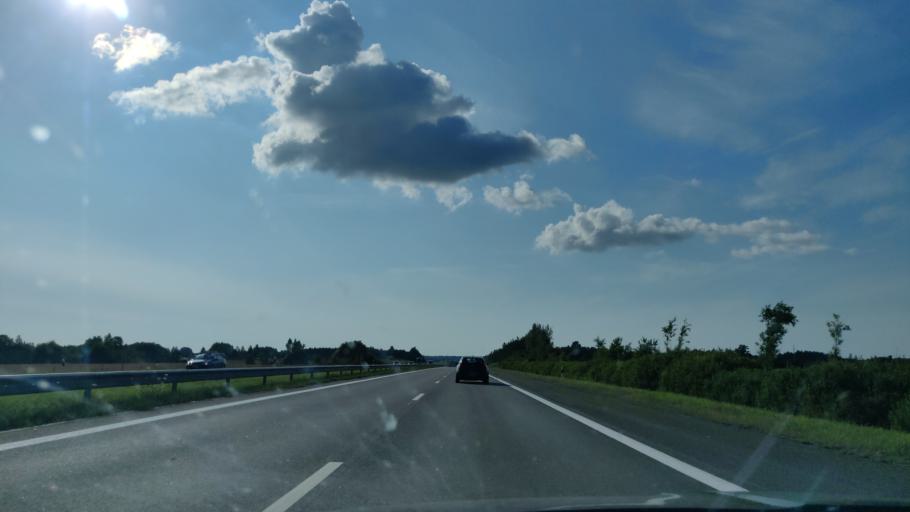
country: LT
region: Klaipedos apskritis
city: Gargzdai
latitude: 55.7209
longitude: 21.4354
